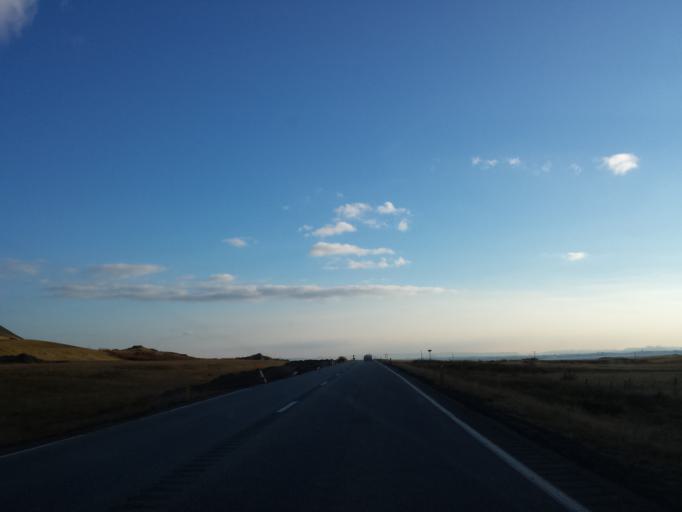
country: IS
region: Capital Region
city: Reykjavik
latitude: 64.2633
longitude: -21.8333
